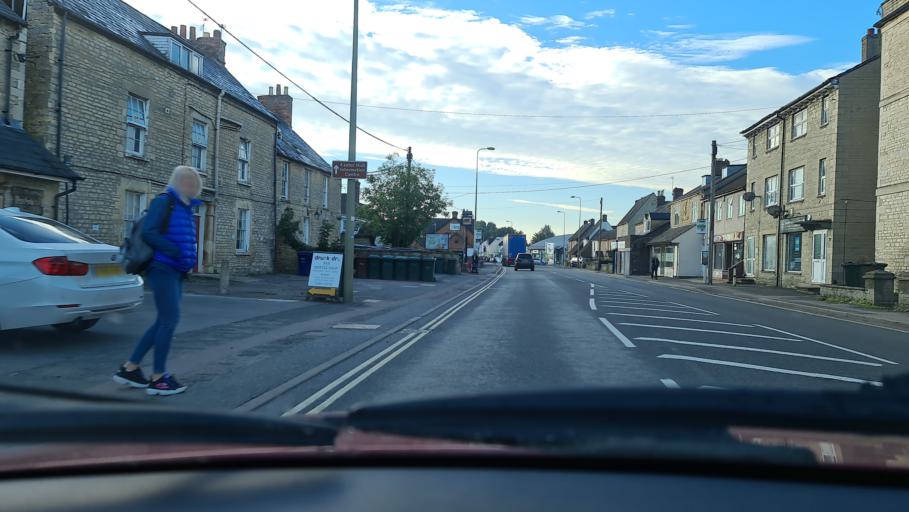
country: GB
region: England
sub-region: Oxfordshire
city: Kidlington
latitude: 51.8241
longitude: -1.2920
